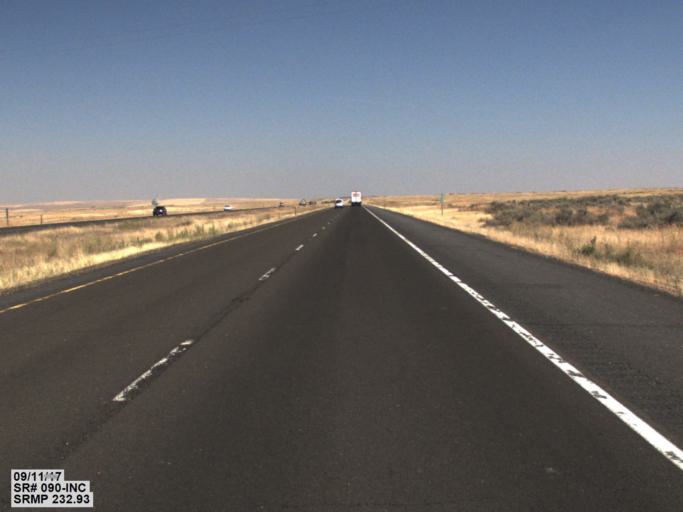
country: US
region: Washington
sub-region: Adams County
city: Ritzville
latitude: 47.2210
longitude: -118.1936
